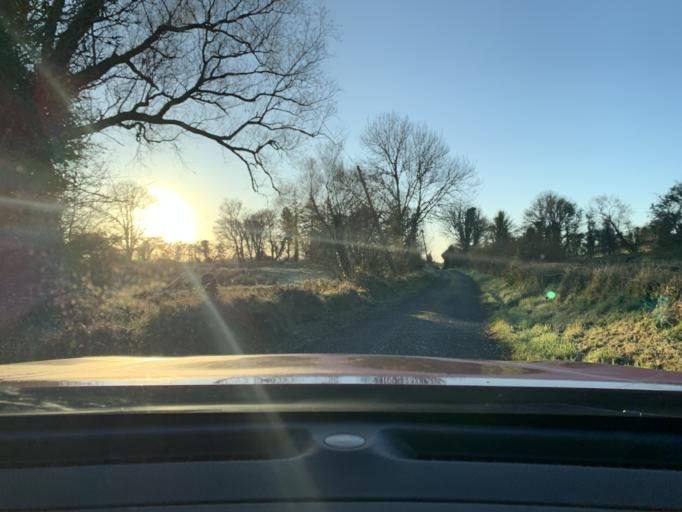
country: IE
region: Connaught
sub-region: Sligo
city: Ballymote
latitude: 54.0617
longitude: -8.5189
